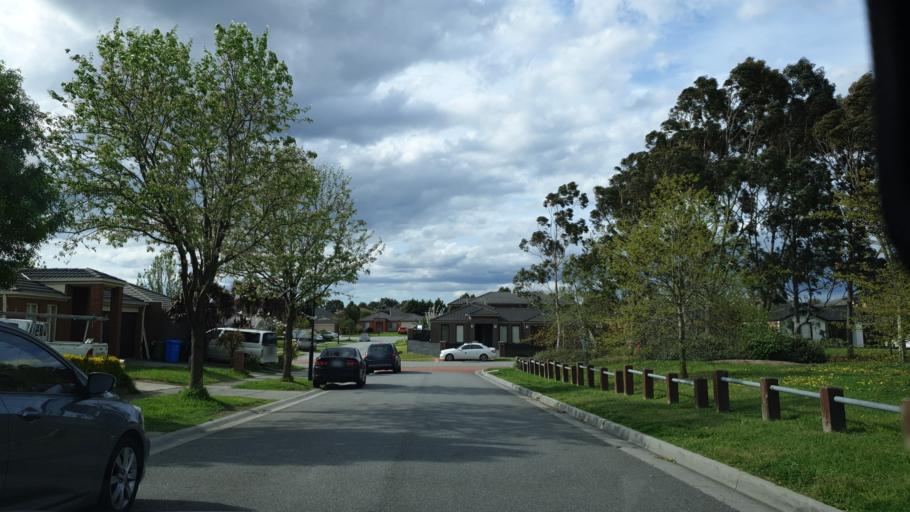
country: AU
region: Victoria
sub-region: Casey
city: Cranbourne North
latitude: -38.0725
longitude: 145.2919
